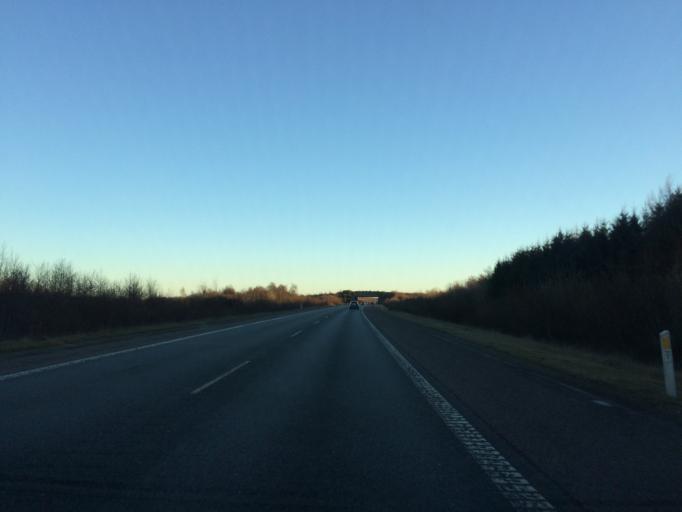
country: DK
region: Central Jutland
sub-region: Herning Kommune
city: Herning
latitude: 56.1798
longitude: 8.9767
